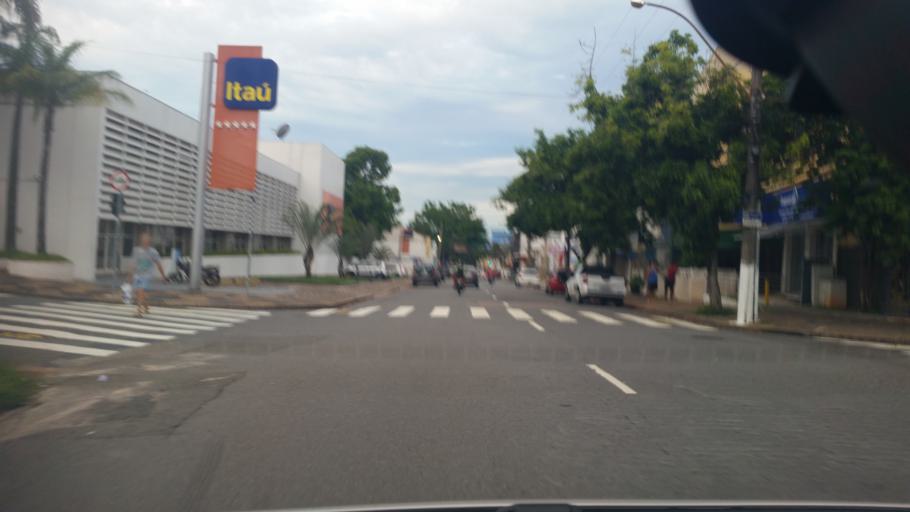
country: BR
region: Sao Paulo
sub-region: Campinas
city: Campinas
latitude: -22.8826
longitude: -47.0518
